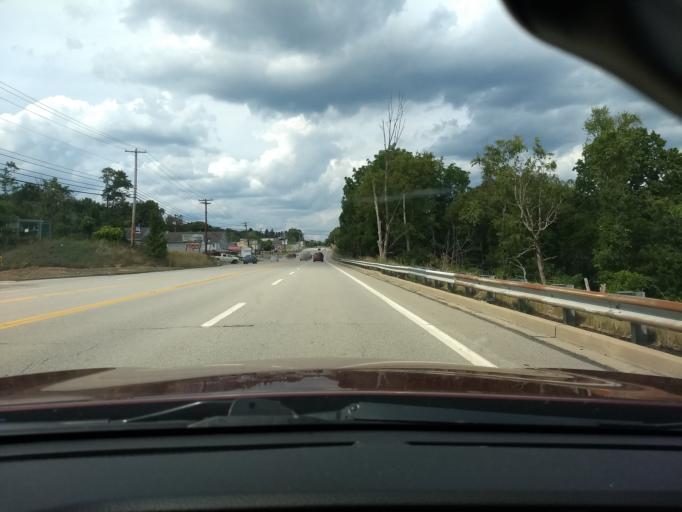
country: US
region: Pennsylvania
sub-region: Armstrong County
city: Freeport
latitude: 40.6477
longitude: -79.7091
